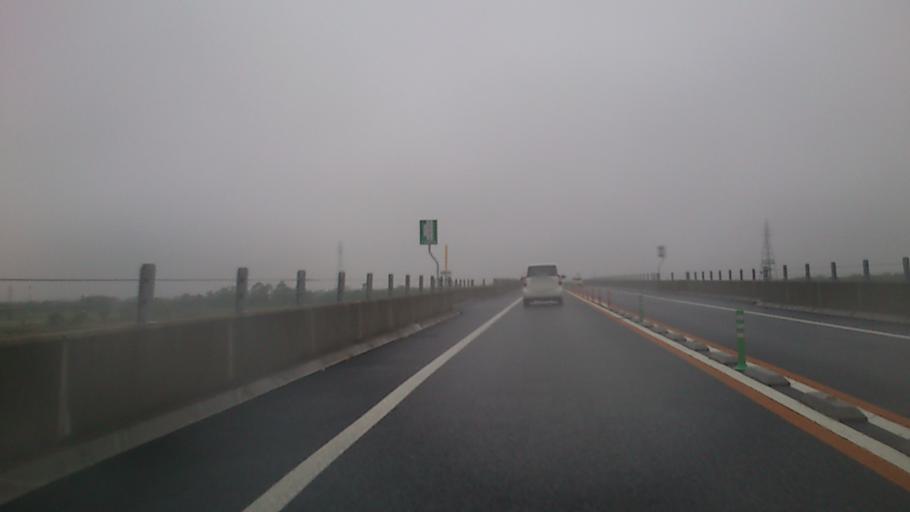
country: JP
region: Hokkaido
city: Kushiro
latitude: 43.0335
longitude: 144.3846
